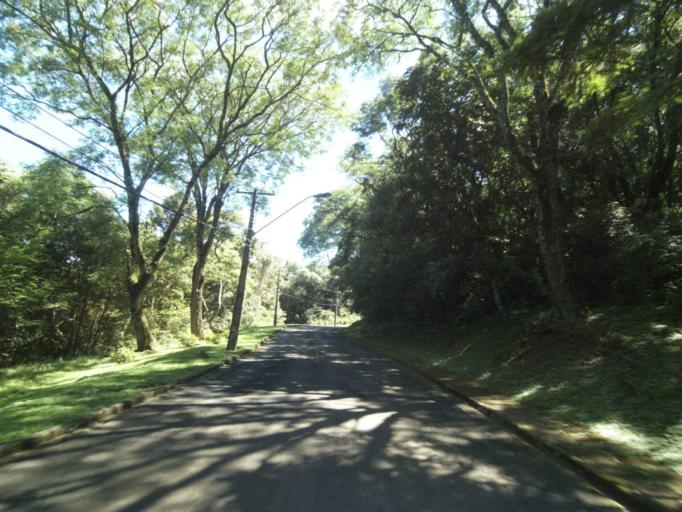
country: BR
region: Parana
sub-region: Chopinzinho
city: Chopinzinho
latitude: -25.7956
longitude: -52.0948
